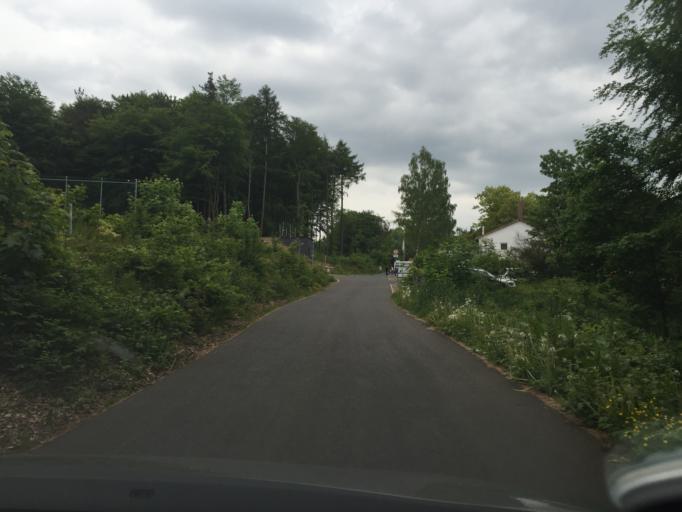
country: DE
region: Bavaria
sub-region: Regierungsbezirk Unterfranken
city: Johannesberg
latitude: 50.0439
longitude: 9.1068
